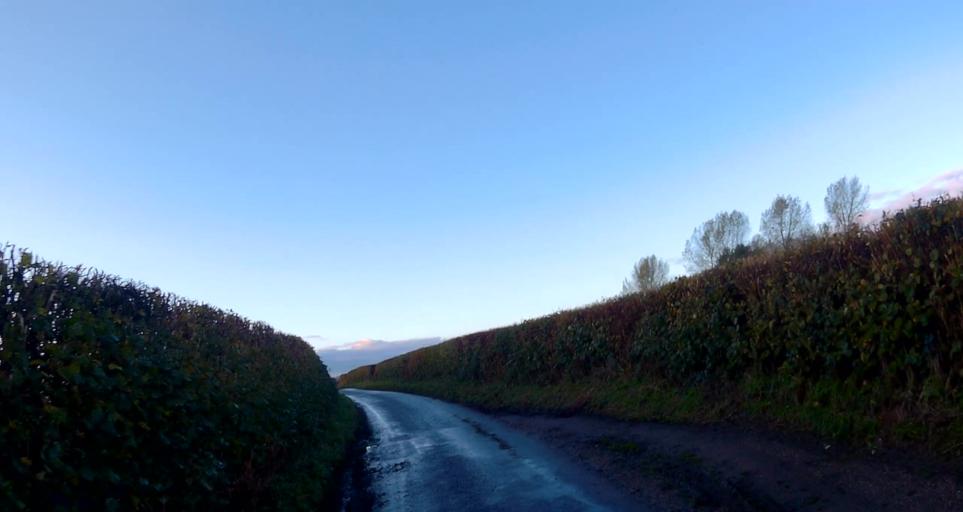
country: GB
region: England
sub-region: Hampshire
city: Basingstoke
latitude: 51.2139
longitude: -1.0901
